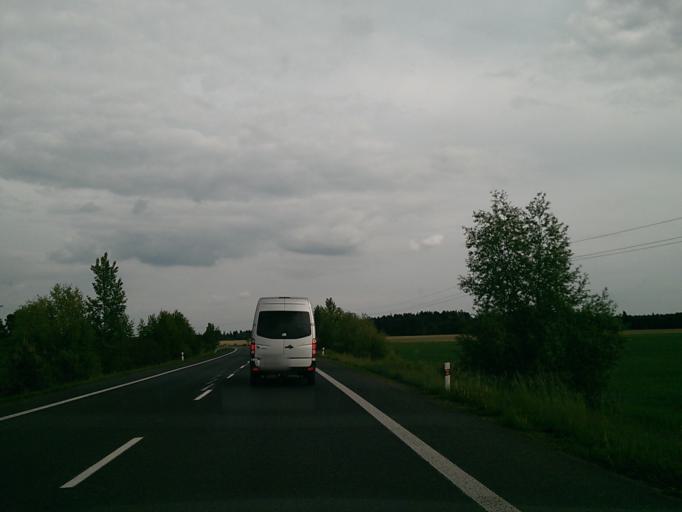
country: CZ
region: Central Bohemia
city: Bela pod Bezdezem
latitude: 50.4982
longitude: 14.7936
